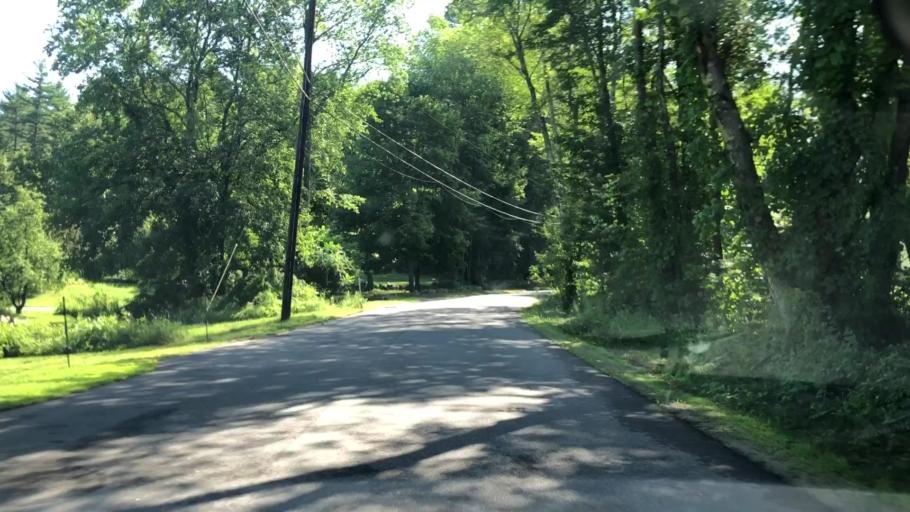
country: US
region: New Hampshire
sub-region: Hillsborough County
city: Milford
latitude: 42.8421
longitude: -71.5953
